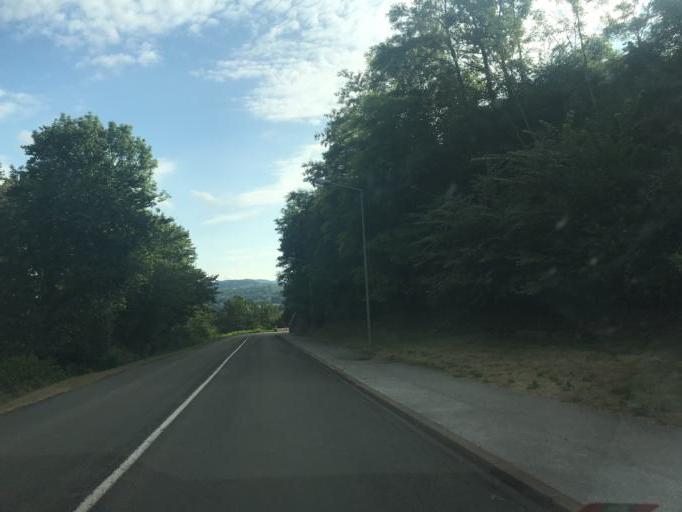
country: FR
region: Franche-Comte
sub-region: Departement du Jura
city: Saint-Lupicin
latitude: 46.3935
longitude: 5.7939
